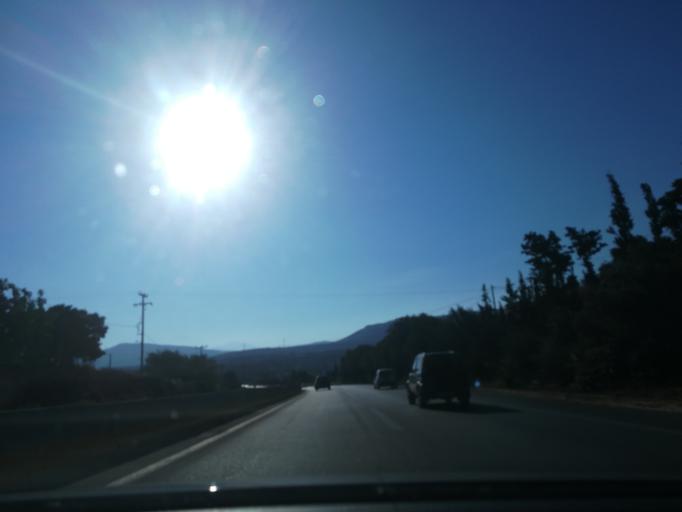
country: GR
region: Crete
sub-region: Nomos Irakleiou
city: Gournes
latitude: 35.3258
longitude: 25.2753
